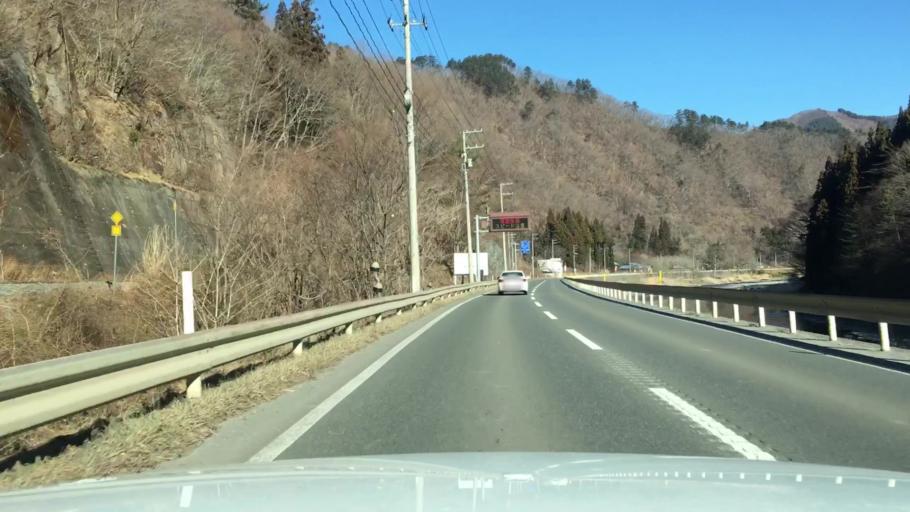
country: JP
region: Iwate
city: Miyako
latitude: 39.6117
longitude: 141.7881
